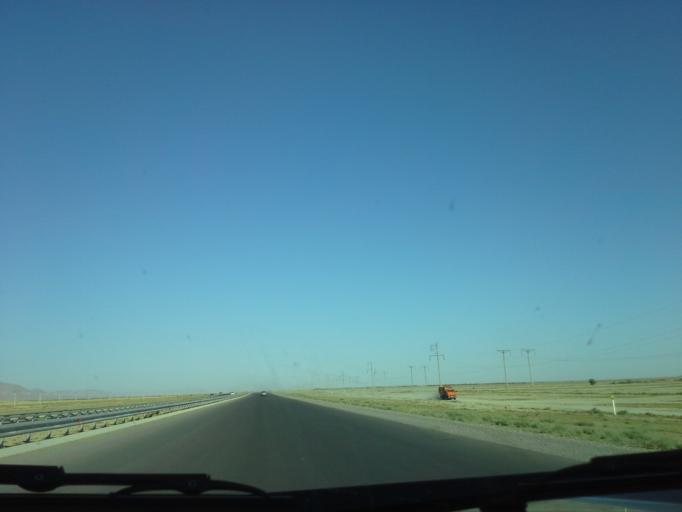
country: TM
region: Balkan
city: Serdar
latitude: 39.0240
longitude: 56.1999
